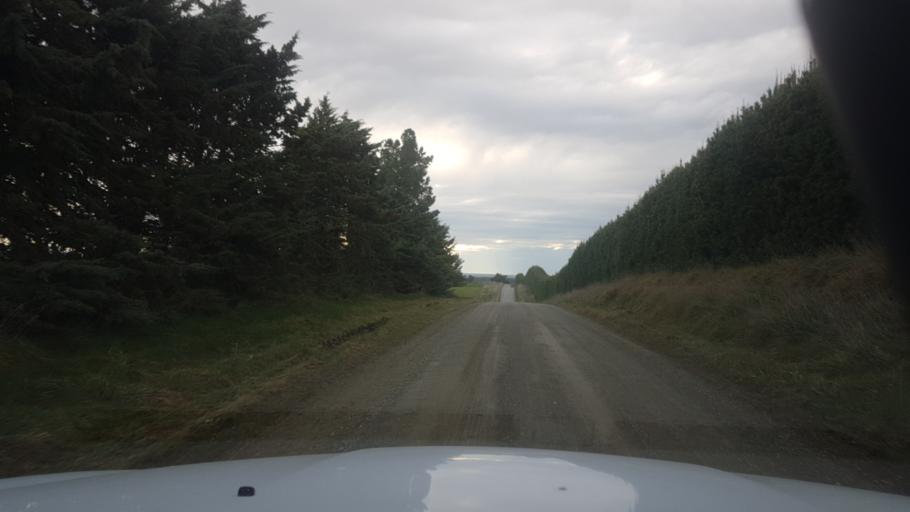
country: NZ
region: Canterbury
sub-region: Timaru District
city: Pleasant Point
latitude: -44.3427
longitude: 171.1405
